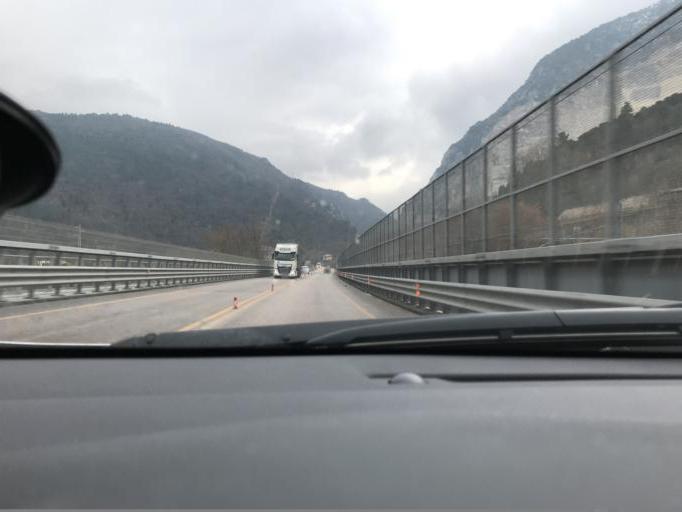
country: IT
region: The Marches
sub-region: Provincia di Ancona
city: Serra San Quirico
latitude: 43.4345
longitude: 13.0182
